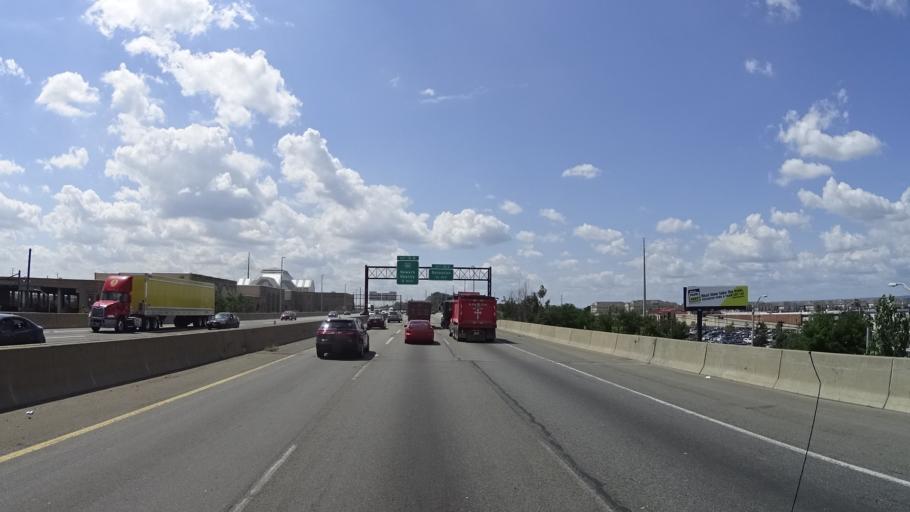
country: US
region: New Jersey
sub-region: Hudson County
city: Secaucus
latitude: 40.7637
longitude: -74.0727
